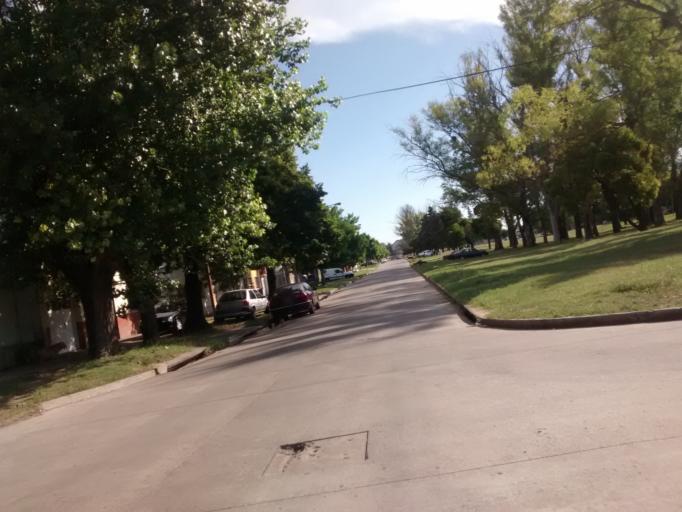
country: AR
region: Buenos Aires
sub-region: Partido de La Plata
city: La Plata
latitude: -34.9511
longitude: -57.9489
